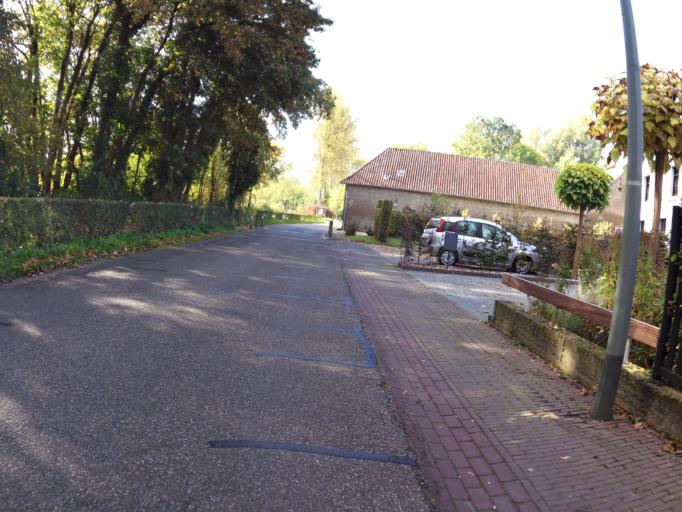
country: NL
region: Limburg
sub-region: Gemeente Schinnen
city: Schinnen
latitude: 50.9460
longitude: 5.8873
